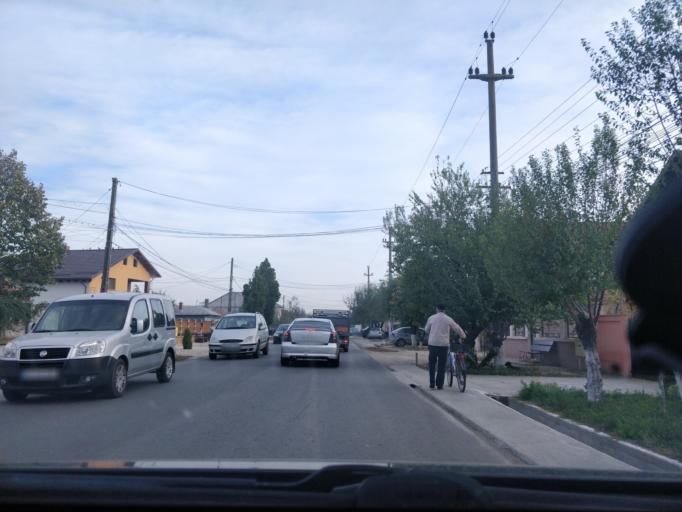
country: RO
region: Giurgiu
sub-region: Comuna Bolintin Vale
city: Malu Spart
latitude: 44.4400
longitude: 25.7182
